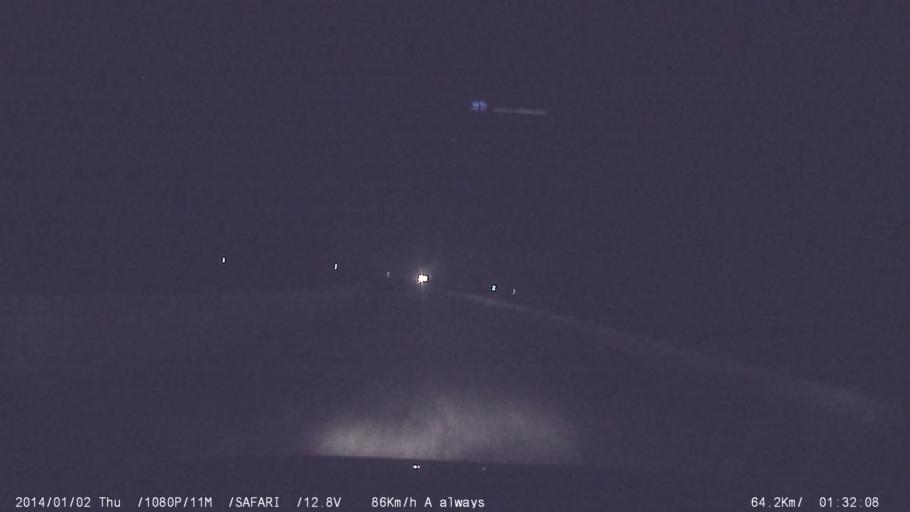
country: IN
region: Tamil Nadu
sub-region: Coimbatore
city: Sulur
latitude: 11.0972
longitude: 77.1557
